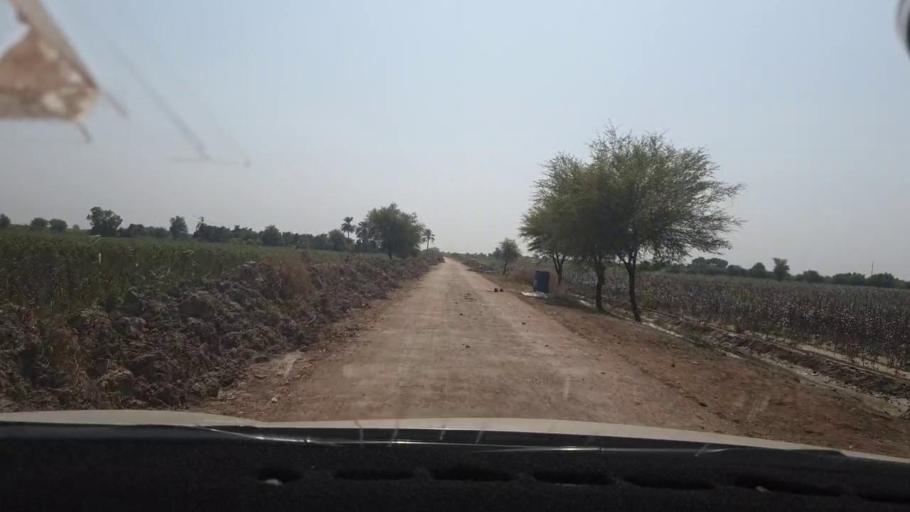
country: PK
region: Sindh
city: Tando Mittha Khan
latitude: 25.9010
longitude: 69.2066
